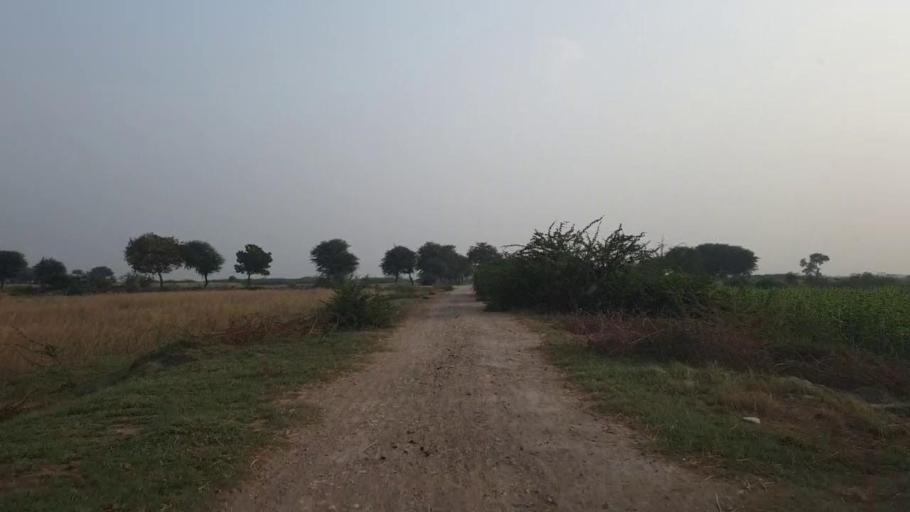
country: PK
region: Sindh
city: Mirpur Batoro
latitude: 24.6528
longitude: 68.3726
